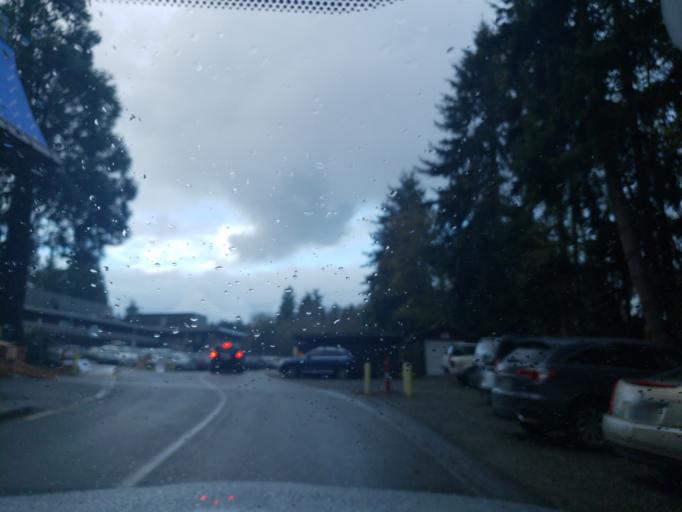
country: US
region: Washington
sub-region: King County
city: Shoreline
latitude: 47.7495
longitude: -122.3587
